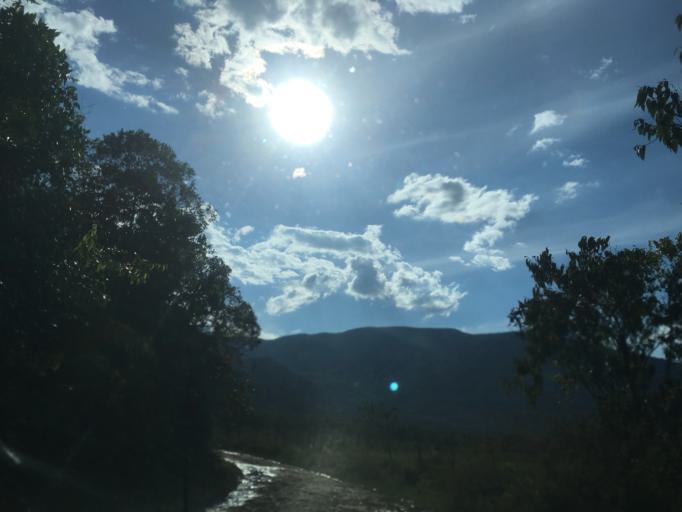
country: CO
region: Santander
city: Oiba
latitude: 6.0976
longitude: -73.1975
